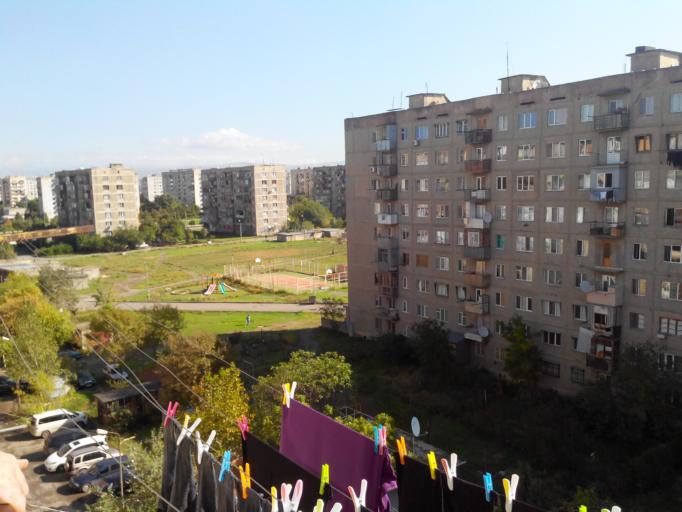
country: GE
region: Kvemo Kartli
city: Rust'avi
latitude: 41.5680
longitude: 44.9750
